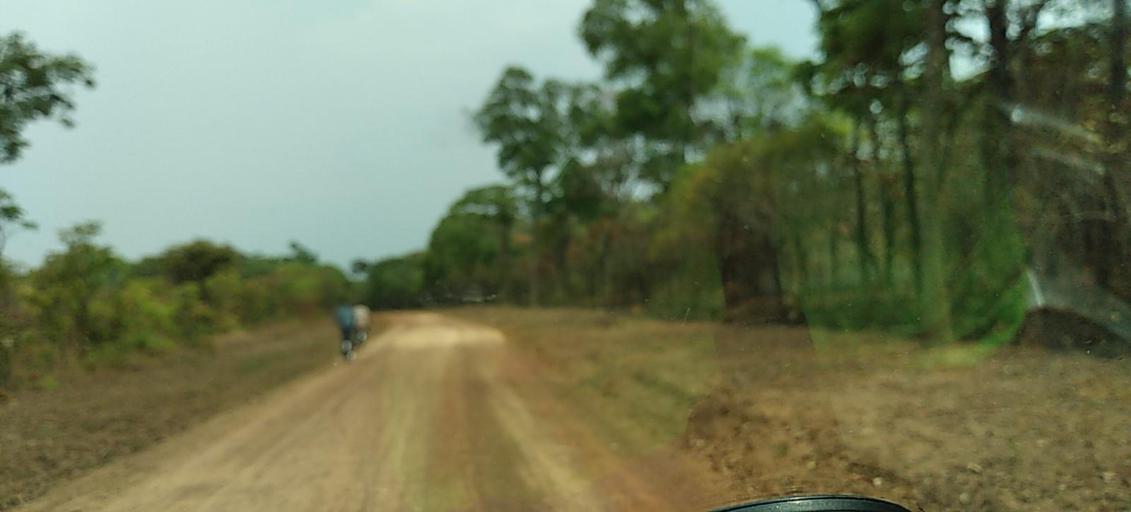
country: ZM
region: North-Western
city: Solwezi
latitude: -12.9493
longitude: 26.5604
